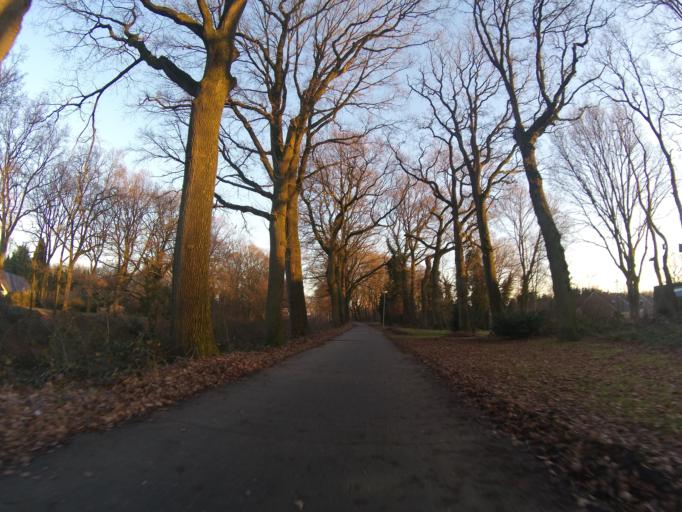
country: NL
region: Drenthe
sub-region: Gemeente Emmen
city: Emmen
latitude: 52.7494
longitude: 6.9023
